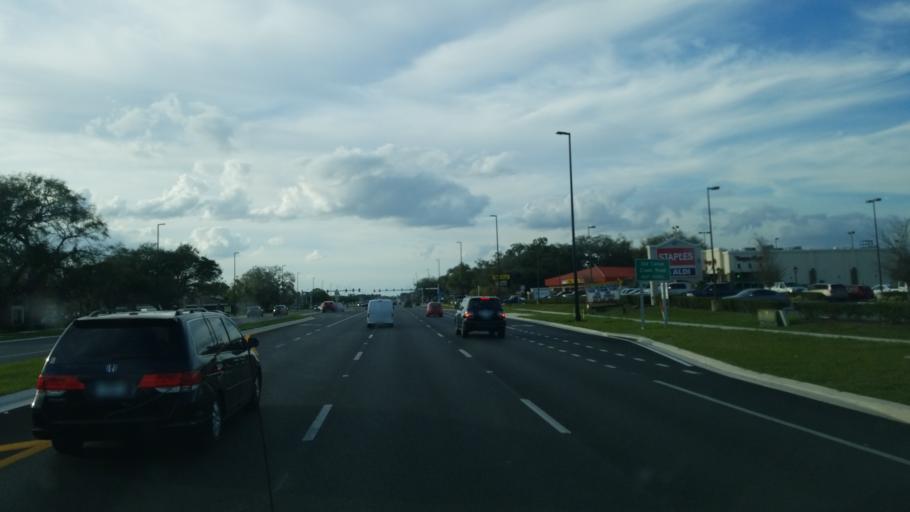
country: US
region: Florida
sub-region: Osceola County
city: Saint Cloud
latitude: 28.2507
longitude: -81.3124
